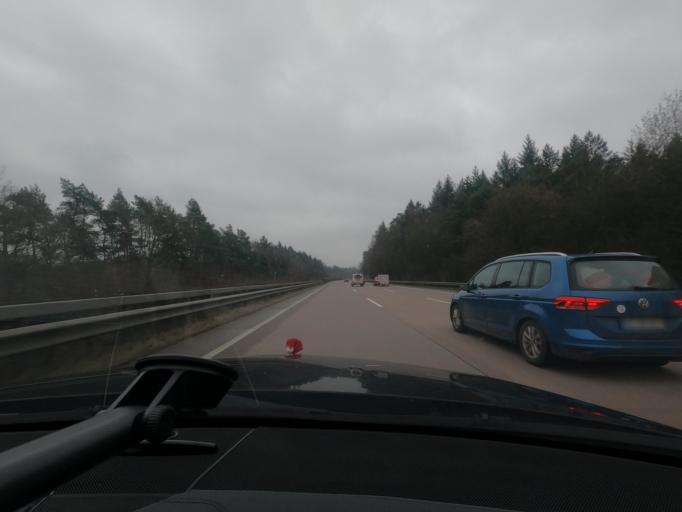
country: DE
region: Lower Saxony
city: Toppenstedt
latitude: 53.2649
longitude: 10.0866
